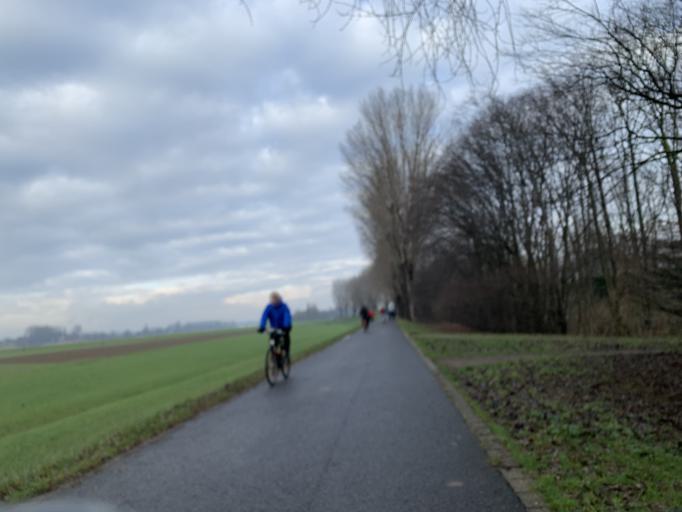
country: DE
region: North Rhine-Westphalia
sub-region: Regierungsbezirk Dusseldorf
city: Meerbusch
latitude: 51.2862
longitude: 6.7240
